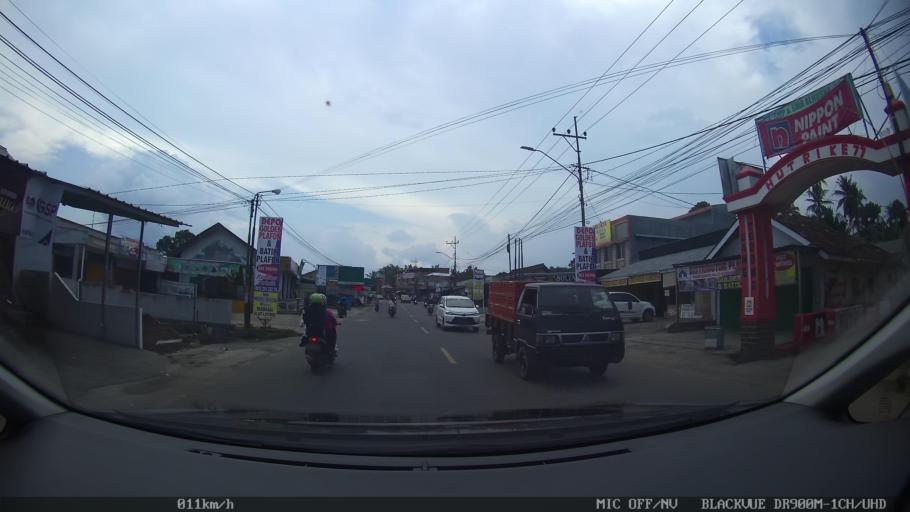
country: ID
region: Lampung
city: Kedaton
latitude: -5.3907
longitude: 105.2118
